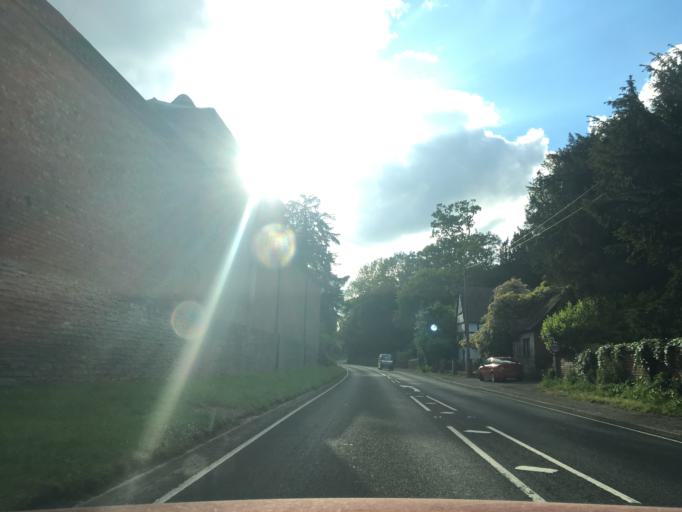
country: GB
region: England
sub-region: Worcestershire
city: Fernhill Heath
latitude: 52.1837
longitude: -2.1532
